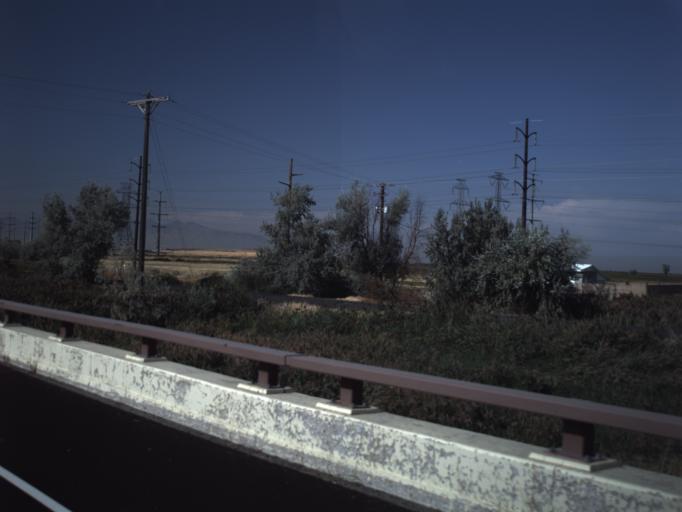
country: US
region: Utah
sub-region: Davis County
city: Centerville
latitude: 40.9260
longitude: -111.8993
